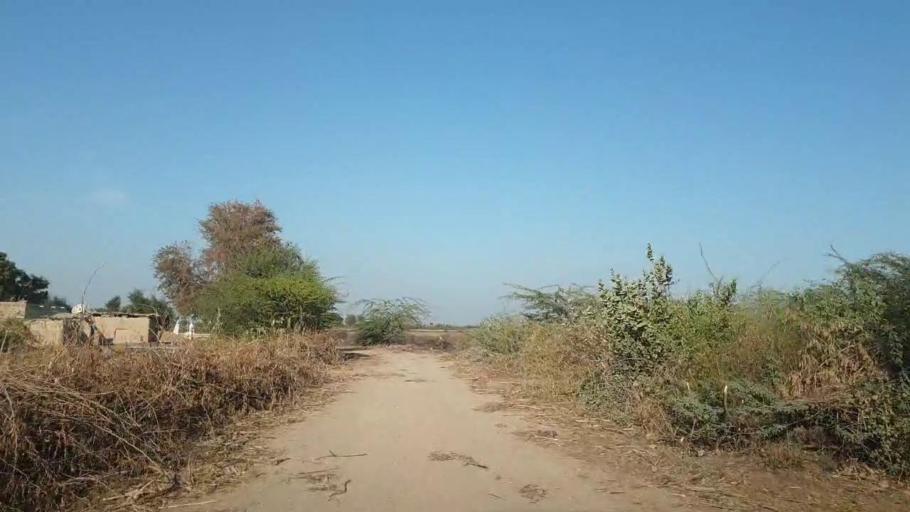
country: PK
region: Sindh
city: Tando Adam
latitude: 25.6898
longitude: 68.6945
